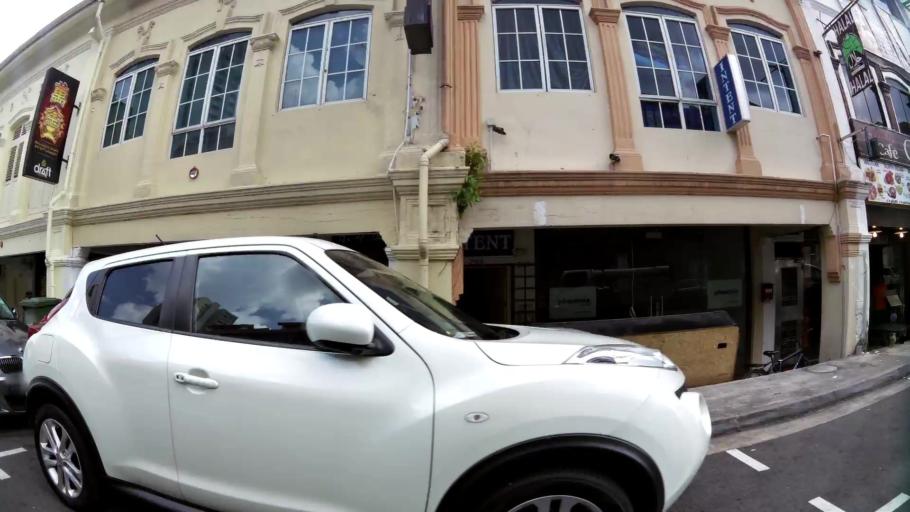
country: SG
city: Singapore
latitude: 1.3078
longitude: 103.8575
